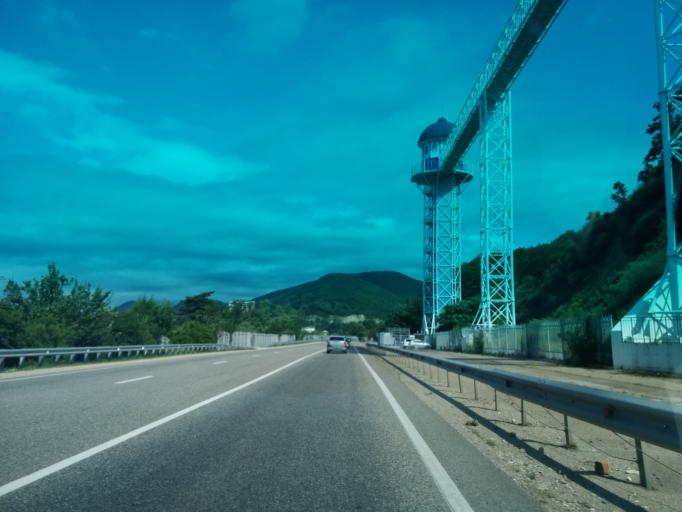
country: RU
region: Krasnodarskiy
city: Nebug
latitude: 44.1571
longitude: 39.0039
